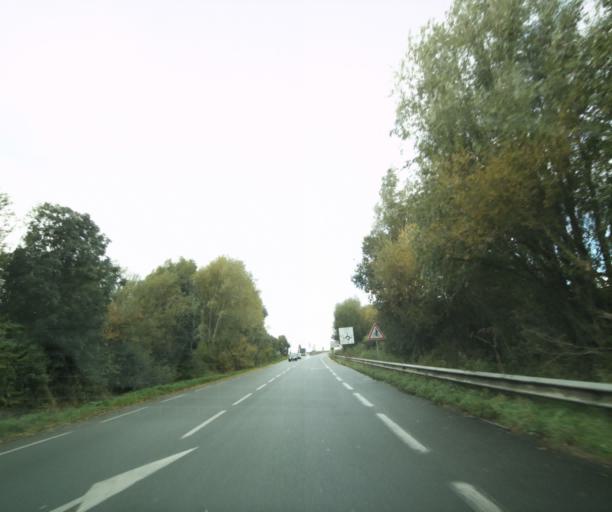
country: FR
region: Nord-Pas-de-Calais
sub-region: Departement du Nord
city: Roncq
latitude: 50.7691
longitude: 3.1079
